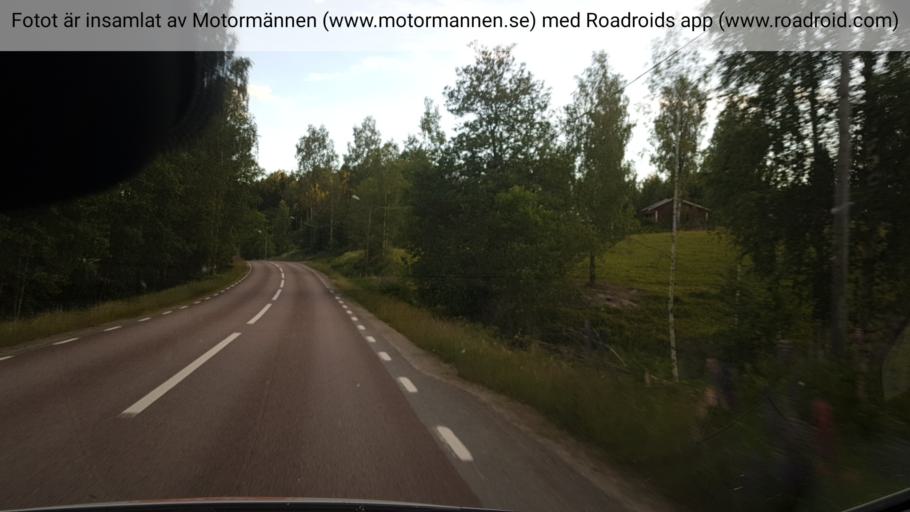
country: SE
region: Vaermland
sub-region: Sunne Kommun
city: Sunne
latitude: 59.6730
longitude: 13.0235
